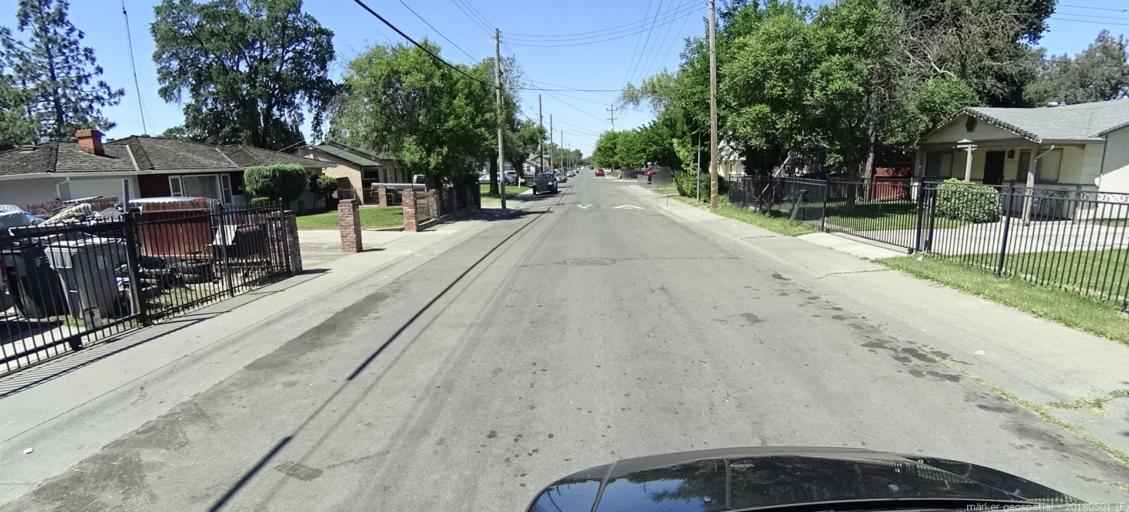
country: US
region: California
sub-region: Sacramento County
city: Rio Linda
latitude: 38.6317
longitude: -121.4419
